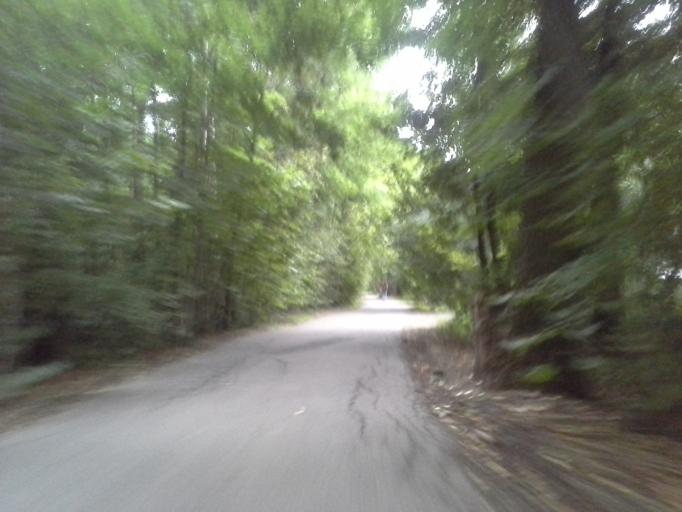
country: RU
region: Moskovskaya
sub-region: Leninskiy Rayon
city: Vnukovo
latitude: 55.6397
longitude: 37.2808
